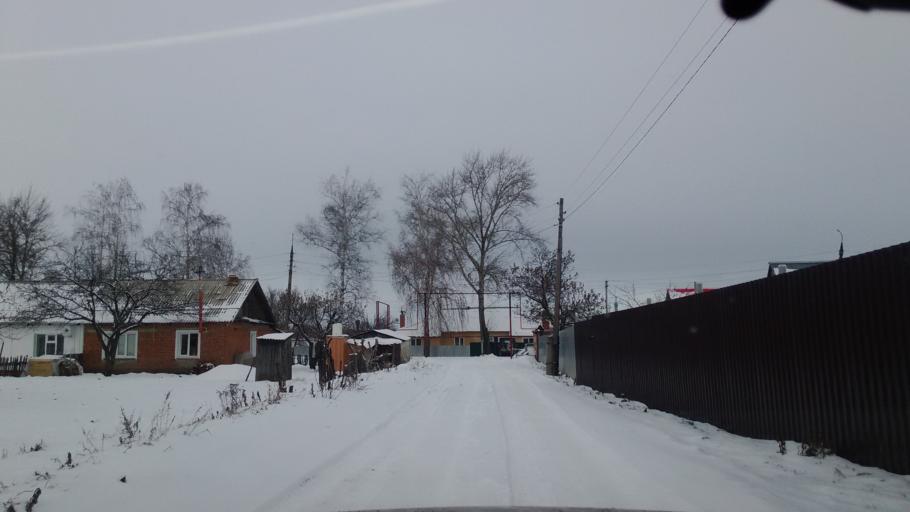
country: RU
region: Tula
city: Bogoroditsk
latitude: 53.7576
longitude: 38.1128
